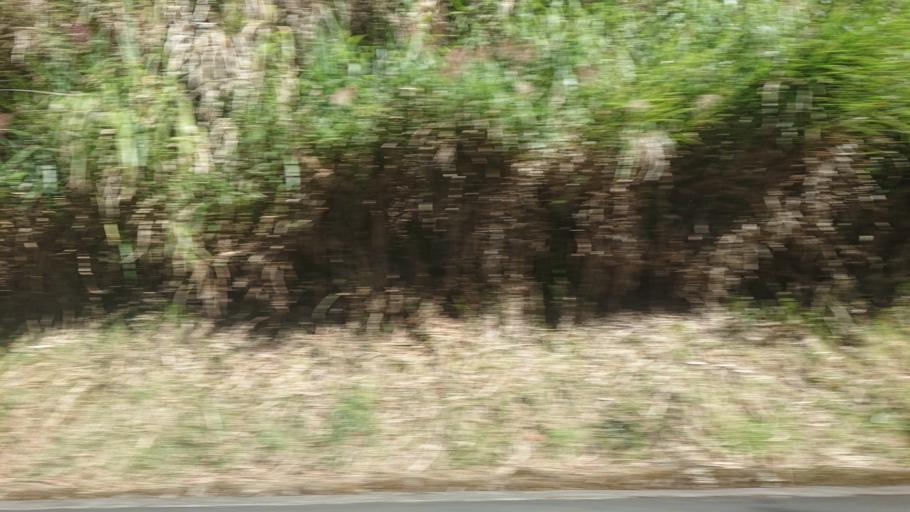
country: TW
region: Taiwan
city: Lugu
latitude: 23.5026
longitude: 120.7988
